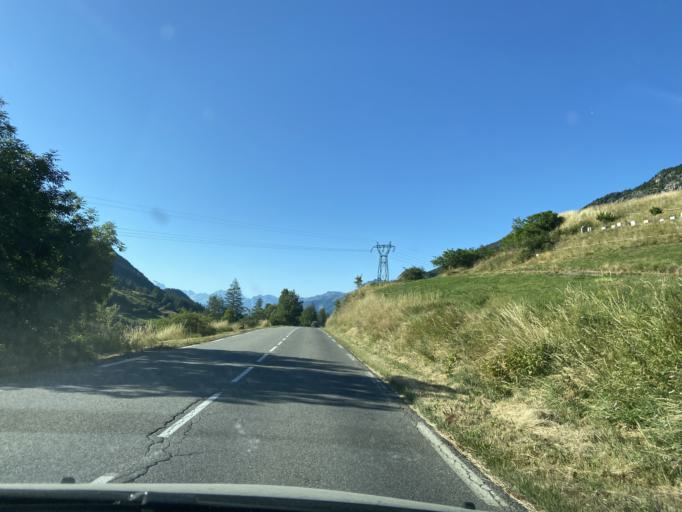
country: FR
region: Provence-Alpes-Cote d'Azur
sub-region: Departement des Hautes-Alpes
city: Guillestre
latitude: 44.6005
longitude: 6.6896
